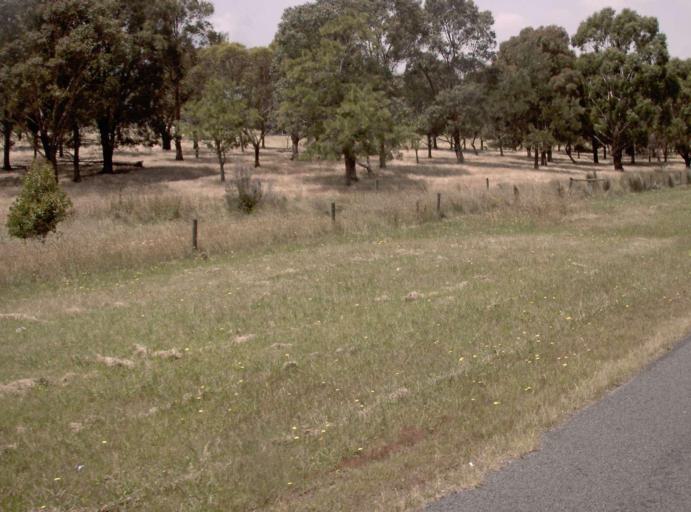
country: AU
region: Victoria
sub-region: Latrobe
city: Traralgon
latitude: -38.2457
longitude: 146.5468
